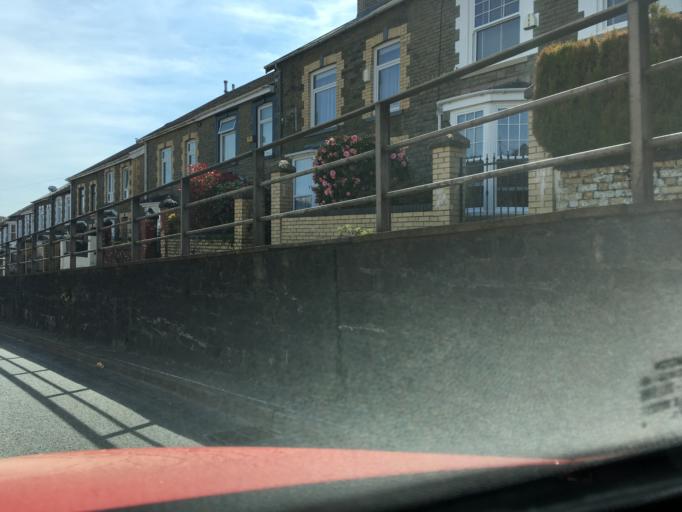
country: GB
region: Wales
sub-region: Merthyr Tydfil County Borough
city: Merthyr Tydfil
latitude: 51.7540
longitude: -3.3764
